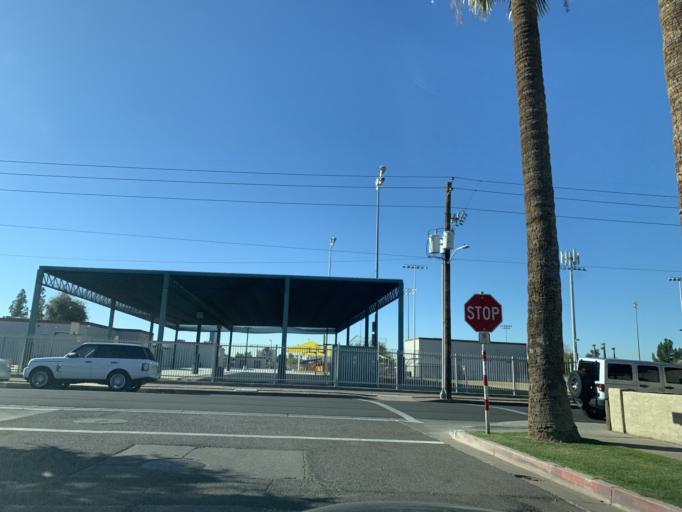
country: US
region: Arizona
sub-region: Maricopa County
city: Phoenix
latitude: 33.4578
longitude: -112.0519
